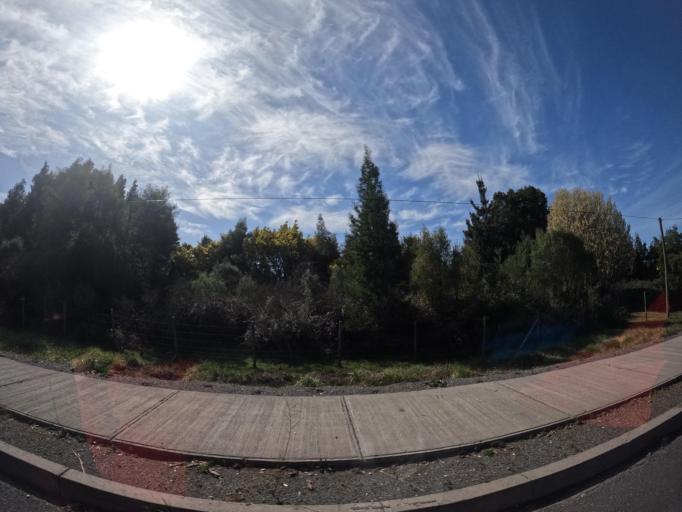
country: CL
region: Biobio
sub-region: Provincia de Biobio
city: Cabrero
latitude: -37.0276
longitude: -72.4423
